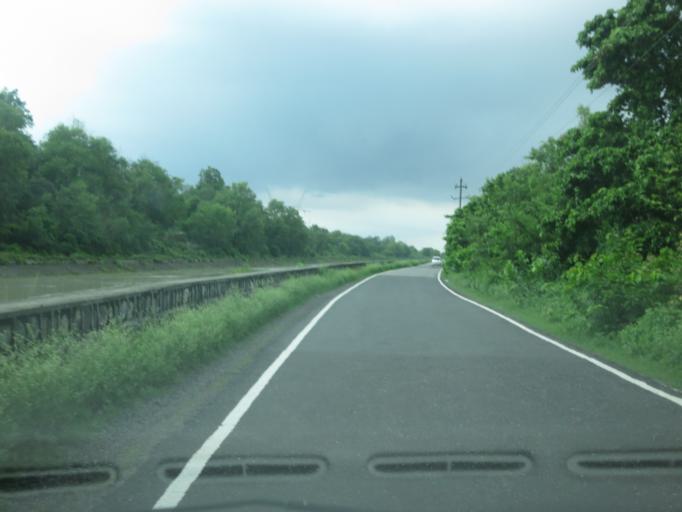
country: IN
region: Uttarakhand
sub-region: Dehradun
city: Raiwala
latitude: 29.9806
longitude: 78.2324
